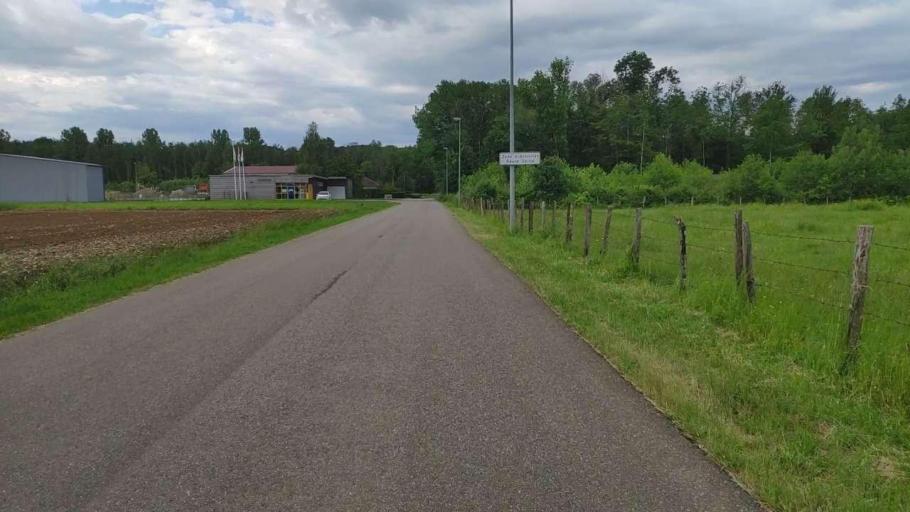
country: FR
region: Franche-Comte
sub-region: Departement du Jura
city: Perrigny
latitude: 46.7593
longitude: 5.5968
